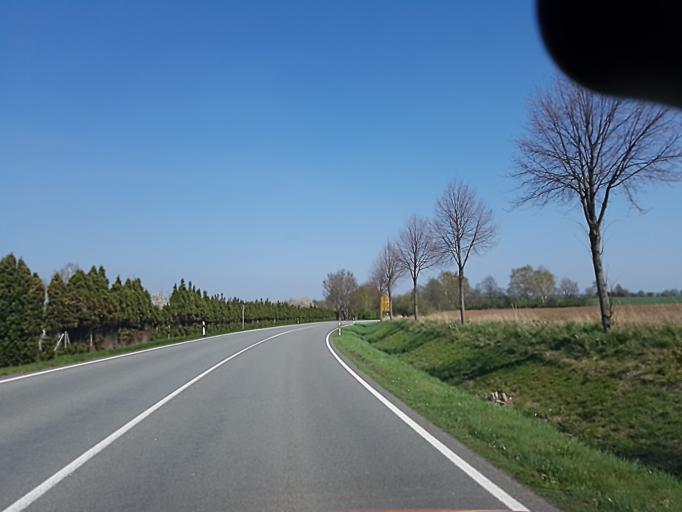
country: DE
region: Saxony
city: Mutzschen
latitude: 51.2534
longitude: 12.8864
